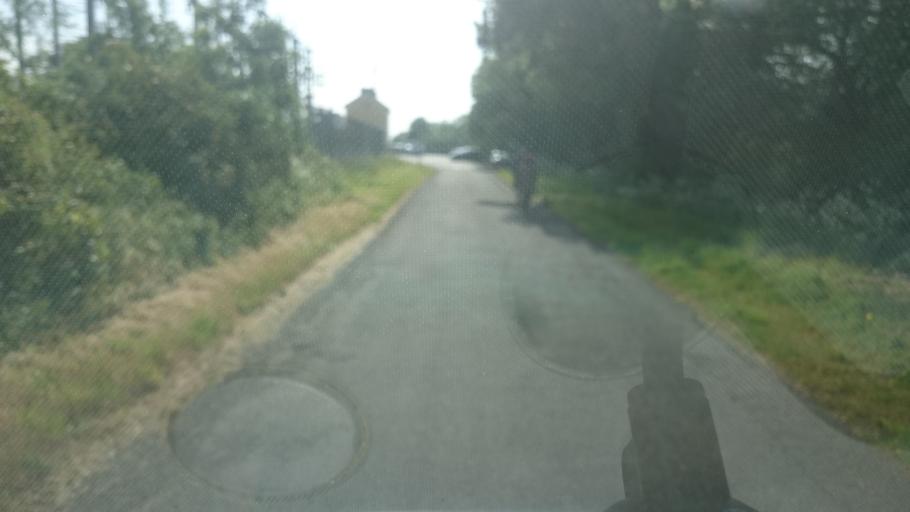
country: FR
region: Pays de la Loire
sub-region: Departement de la Loire-Atlantique
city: Indre
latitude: 47.2044
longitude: -1.6620
